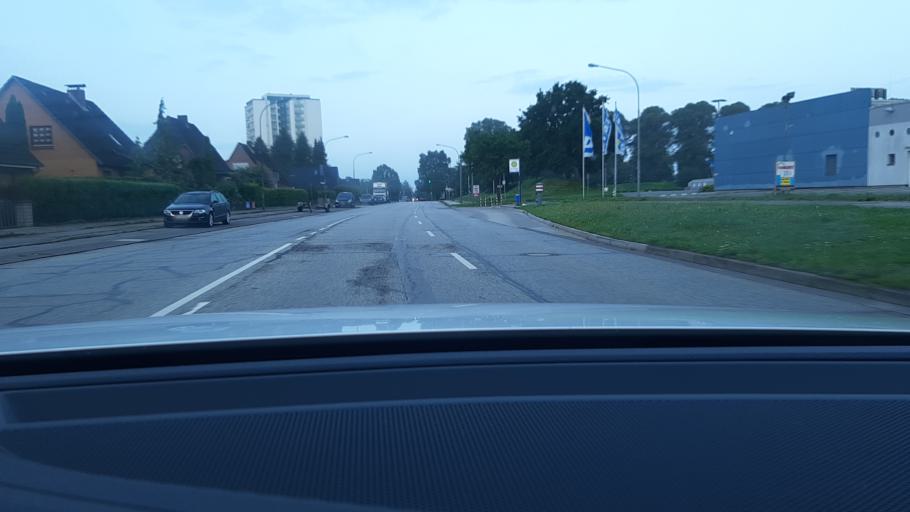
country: DE
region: Schleswig-Holstein
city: Stockelsdorf
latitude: 53.8537
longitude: 10.6365
